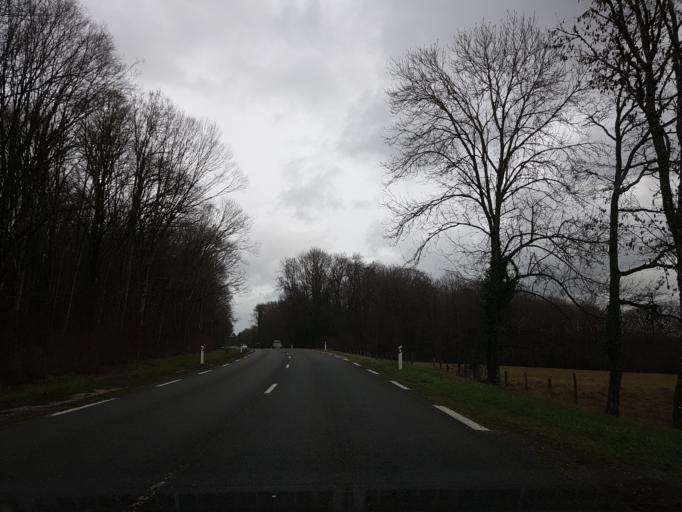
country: FR
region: Champagne-Ardenne
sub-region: Departement de la Haute-Marne
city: Fayl-Billot
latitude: 47.8101
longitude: 5.5309
